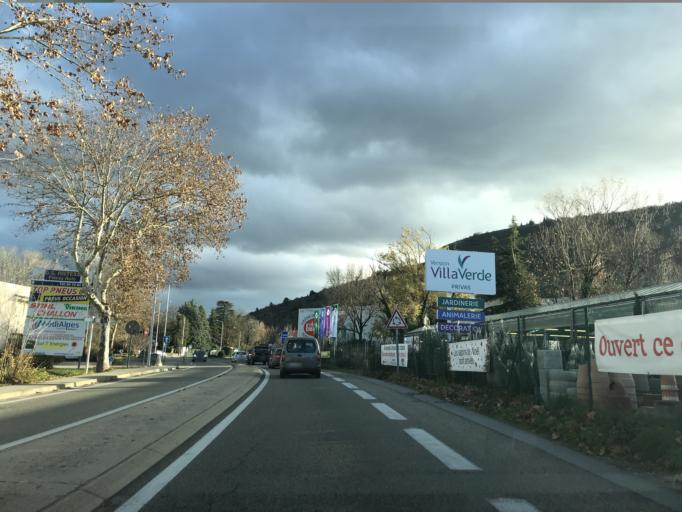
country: FR
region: Rhone-Alpes
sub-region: Departement de l'Ardeche
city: Privas
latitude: 44.7210
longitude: 4.6006
